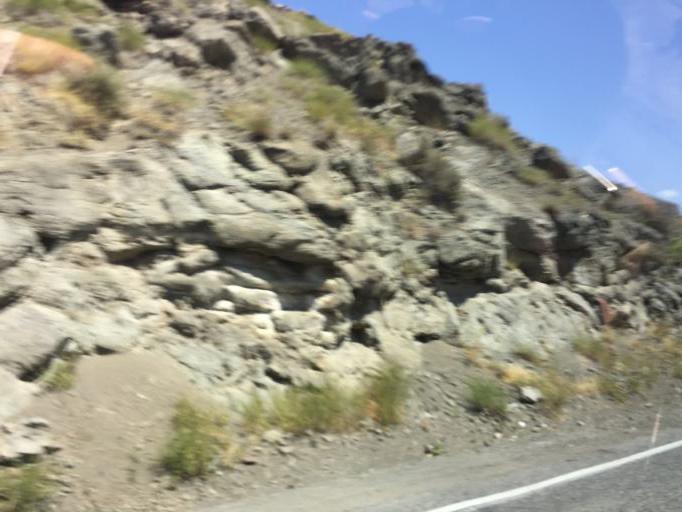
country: AM
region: Vayots' Dzori Marz
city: Zarrit'ap'
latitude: 39.7022
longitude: 45.6033
